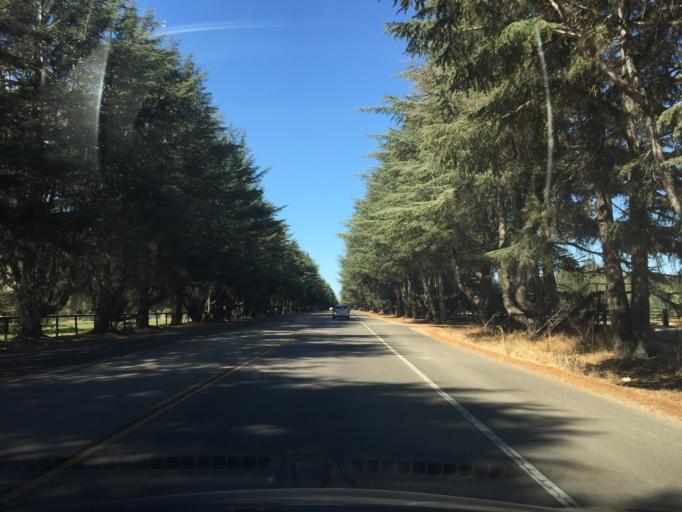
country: US
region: California
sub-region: Santa Barbara County
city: Solvang
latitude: 34.5994
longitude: -120.1604
